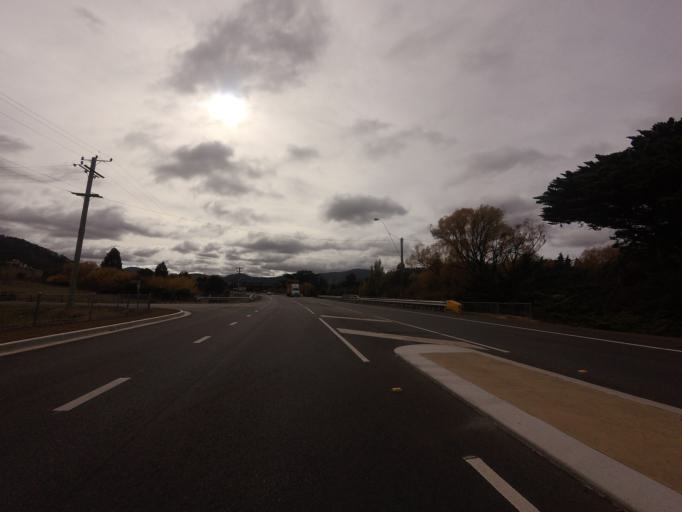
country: AU
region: Tasmania
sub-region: Brighton
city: Bridgewater
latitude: -42.6145
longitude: 147.2228
